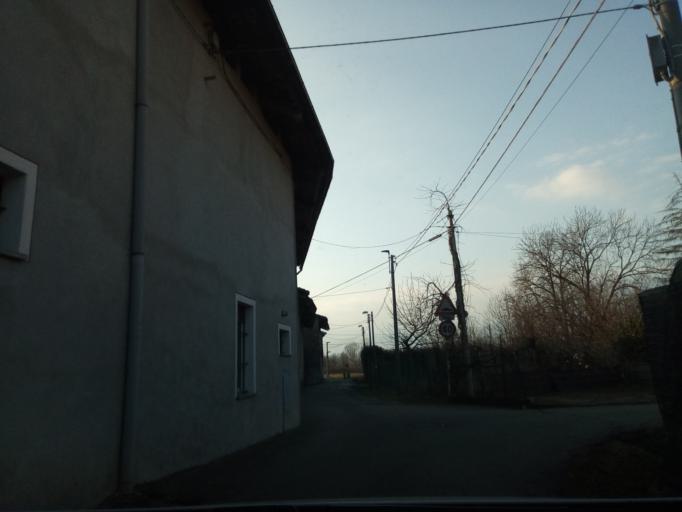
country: IT
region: Piedmont
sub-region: Provincia di Torino
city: Cascinette d'Ivrea
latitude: 45.4663
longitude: 7.9176
